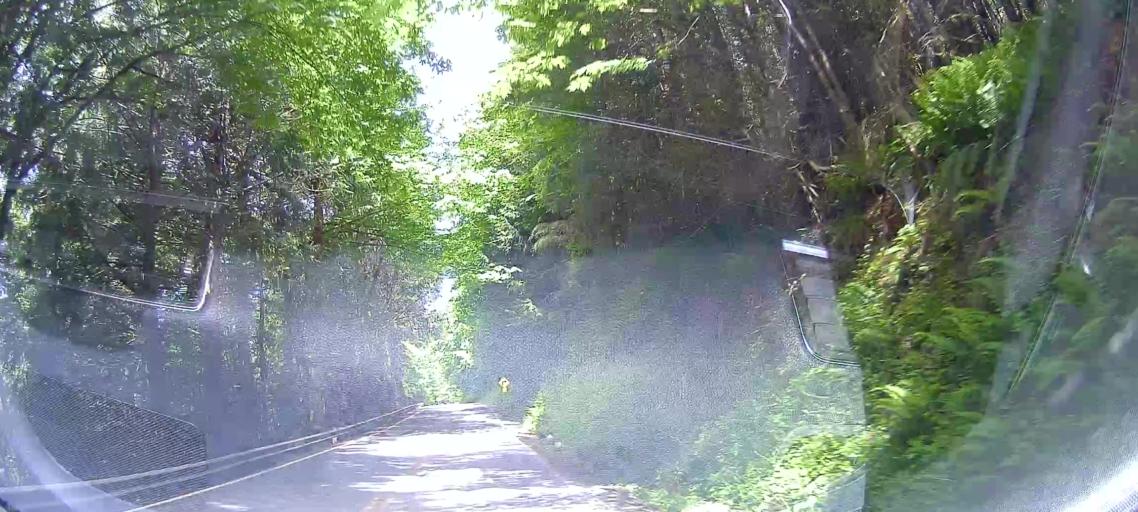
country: US
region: Washington
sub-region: Snohomish County
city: Bryant
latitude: 48.3258
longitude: -122.1629
